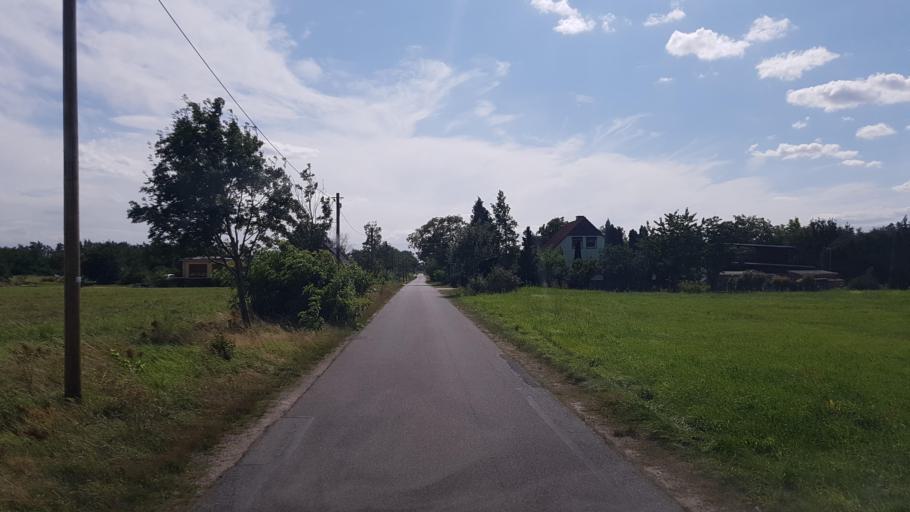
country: DE
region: Brandenburg
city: Muhlberg
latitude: 51.4491
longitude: 13.2946
